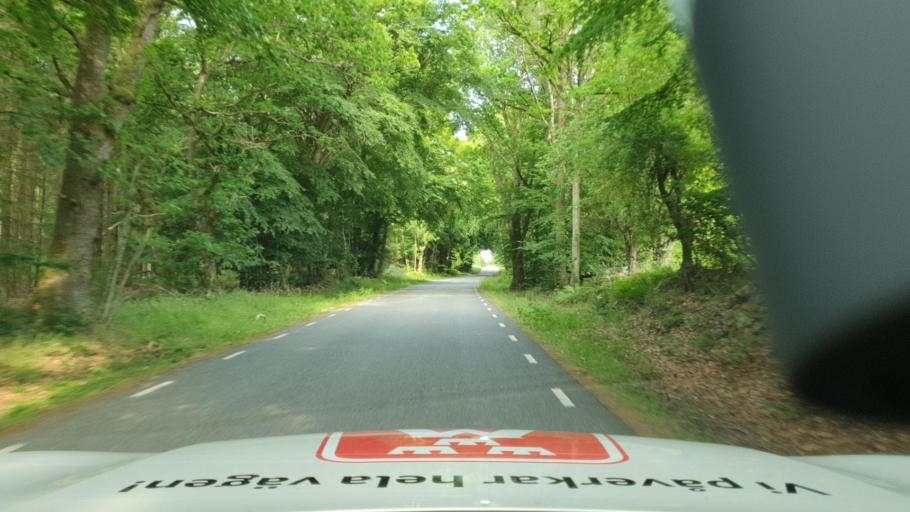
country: SE
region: Skane
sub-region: Kristianstads Kommun
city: Degeberga
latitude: 55.6930
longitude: 14.0694
